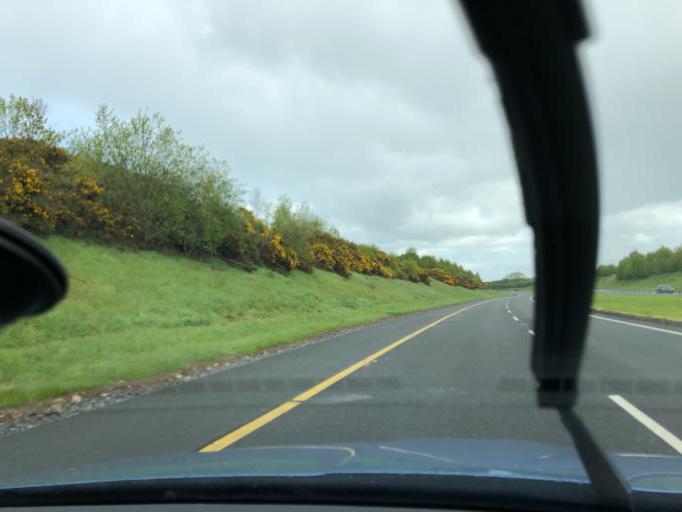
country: IE
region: Munster
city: Cahir
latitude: 52.3799
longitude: -7.9493
